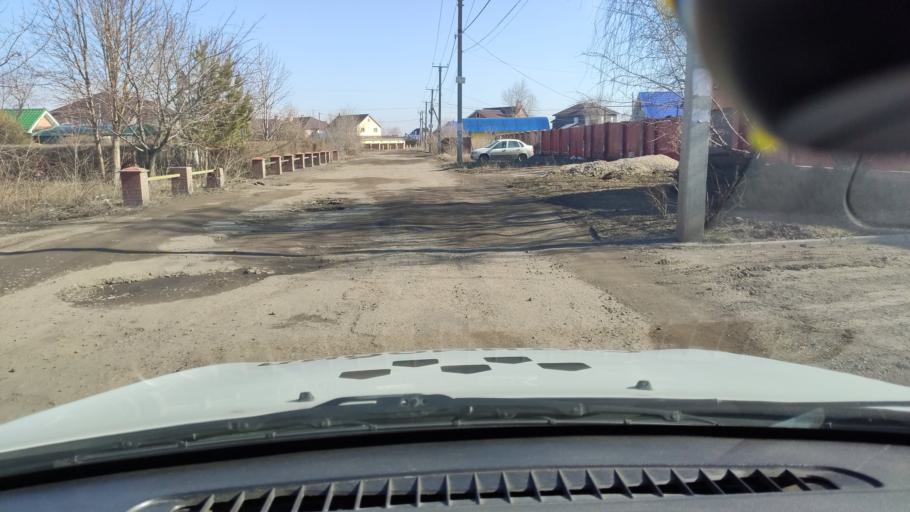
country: RU
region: Samara
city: Tol'yatti
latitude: 53.5546
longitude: 49.3698
